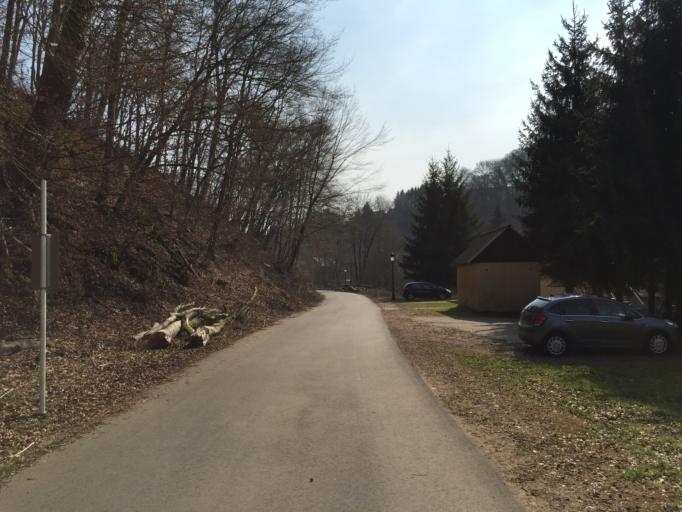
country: LU
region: Luxembourg
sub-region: Canton de Luxembourg
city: Hesperange
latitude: 49.5762
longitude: 6.1544
